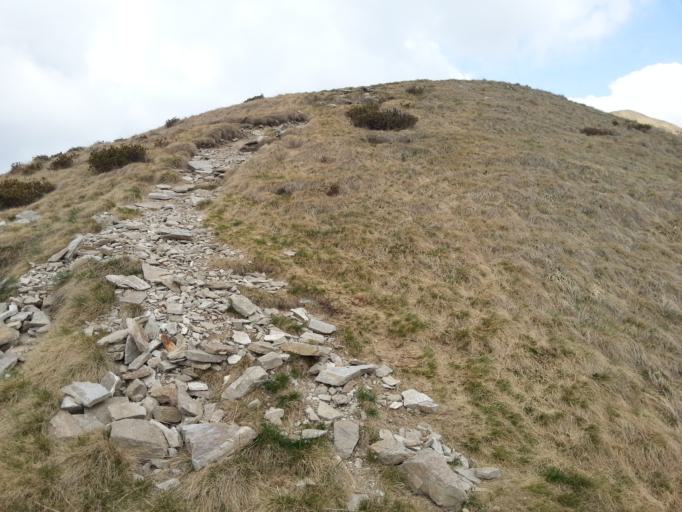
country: IT
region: Lombardy
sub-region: Provincia di Varese
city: Curiglia
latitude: 46.0816
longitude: 8.8608
